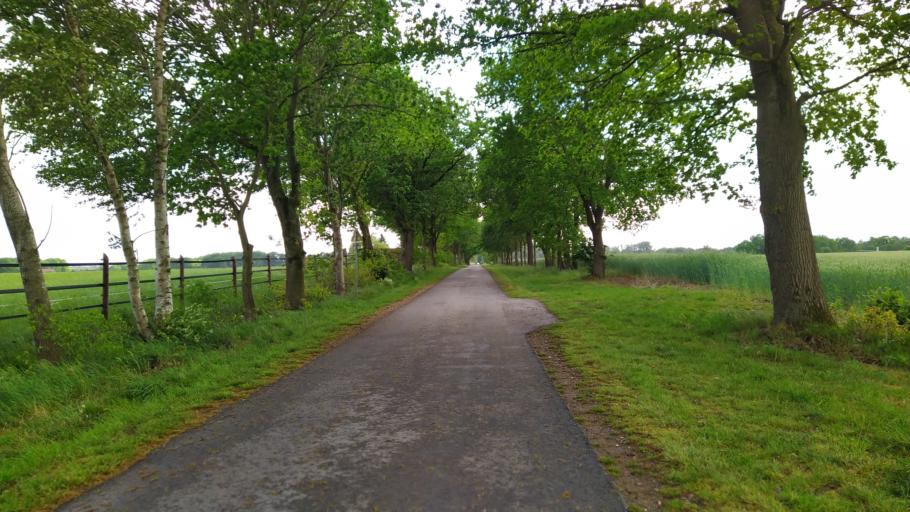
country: DE
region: Lower Saxony
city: Brest
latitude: 53.4405
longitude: 9.3619
